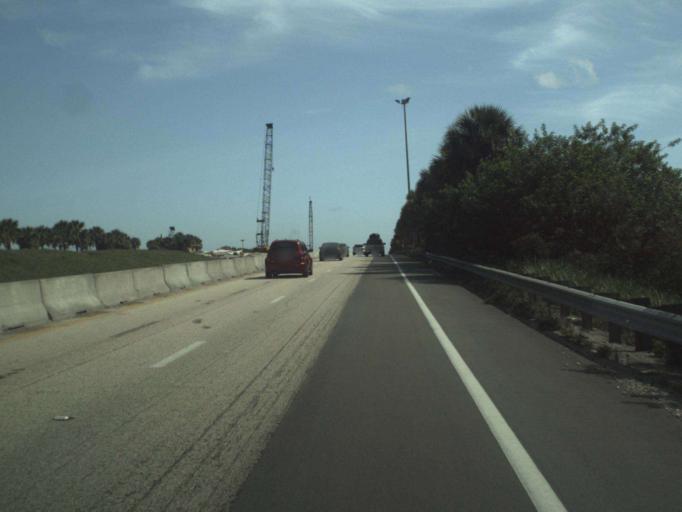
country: US
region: Florida
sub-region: Indian River County
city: Fellsmere
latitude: 27.7649
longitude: -80.5510
